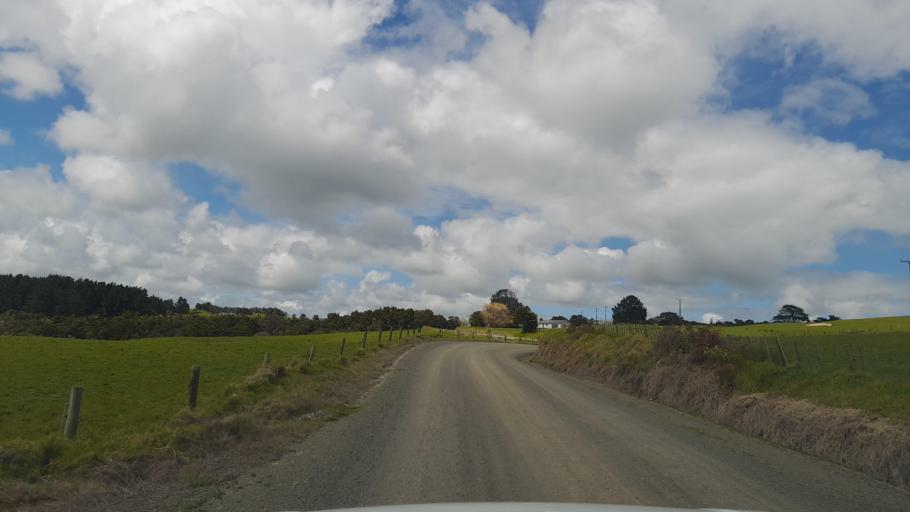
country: NZ
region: Auckland
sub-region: Auckland
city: Wellsford
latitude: -36.1955
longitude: 174.3355
